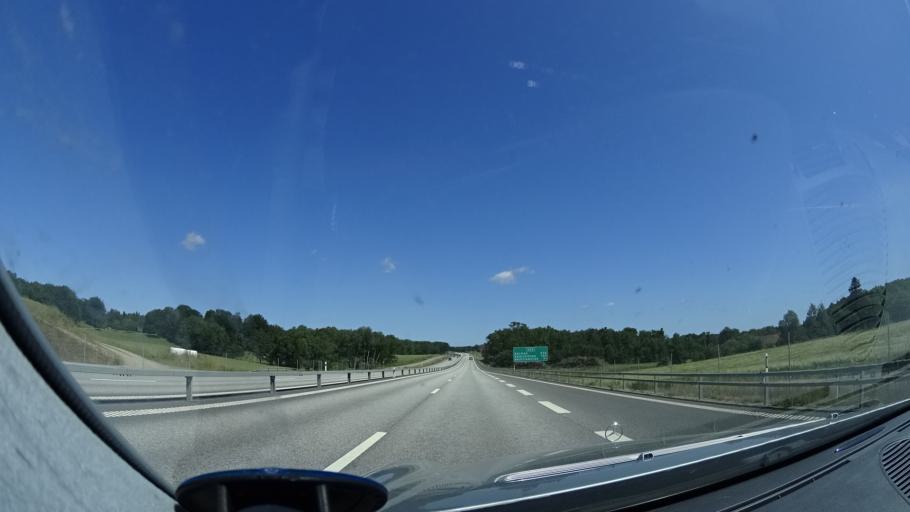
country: SE
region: Skane
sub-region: Horby Kommun
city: Hoerby
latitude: 55.8694
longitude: 13.7000
